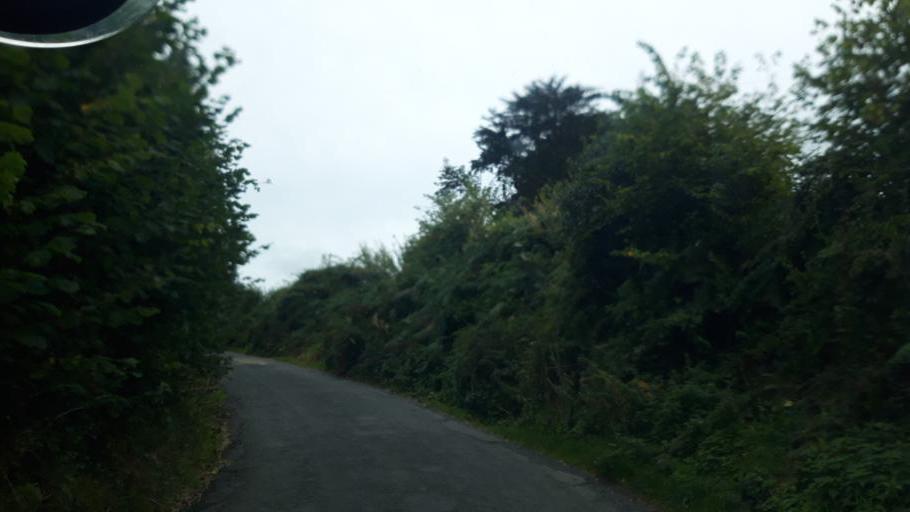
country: IE
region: Leinster
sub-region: Wicklow
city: Enniskerry
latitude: 53.1784
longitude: -6.2045
